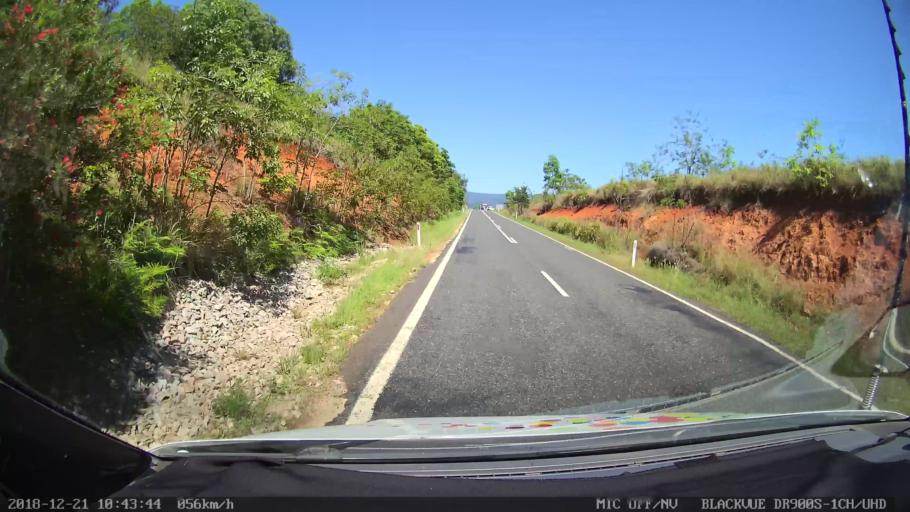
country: AU
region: New South Wales
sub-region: Clarence Valley
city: Gordon
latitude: -29.5770
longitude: 152.5530
